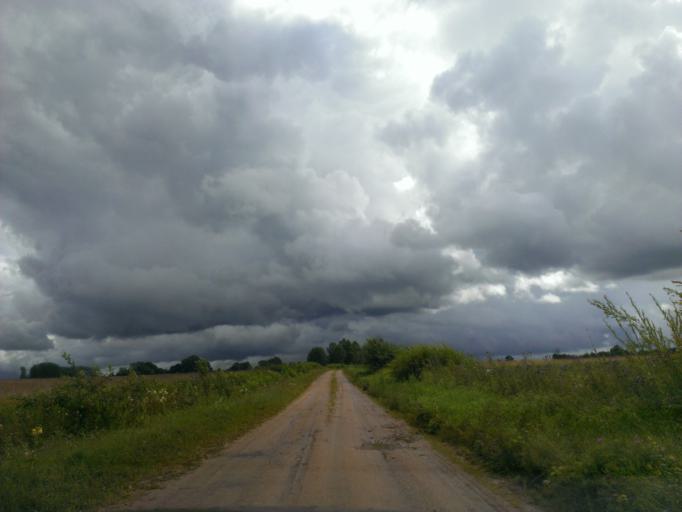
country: LV
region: Sigulda
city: Sigulda
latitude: 57.2107
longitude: 24.9441
